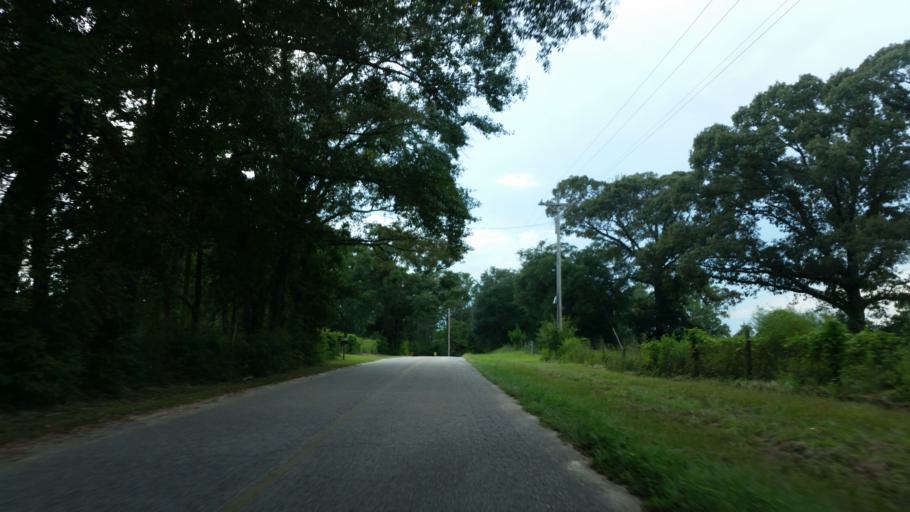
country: US
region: Florida
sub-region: Santa Rosa County
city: Point Baker
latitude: 30.7340
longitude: -86.8898
